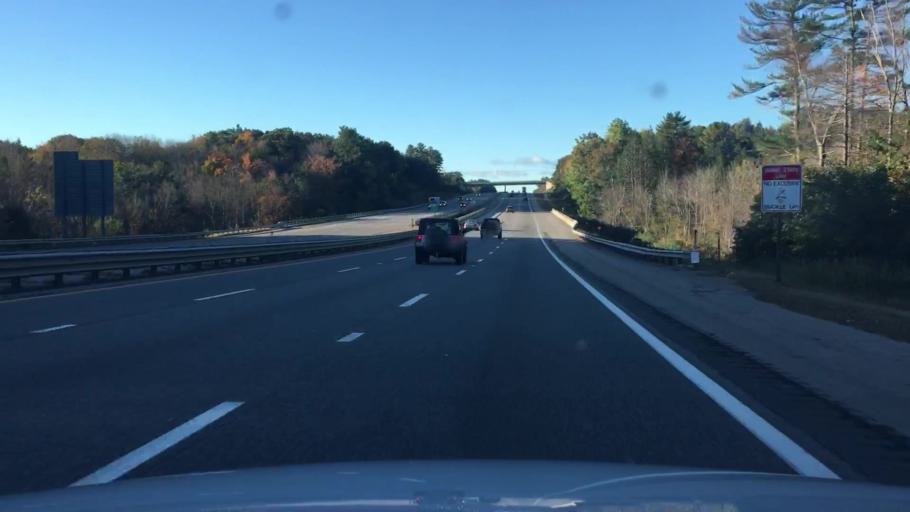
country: US
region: Maine
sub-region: York County
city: West Kennebunk
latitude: 43.4017
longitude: -70.5647
